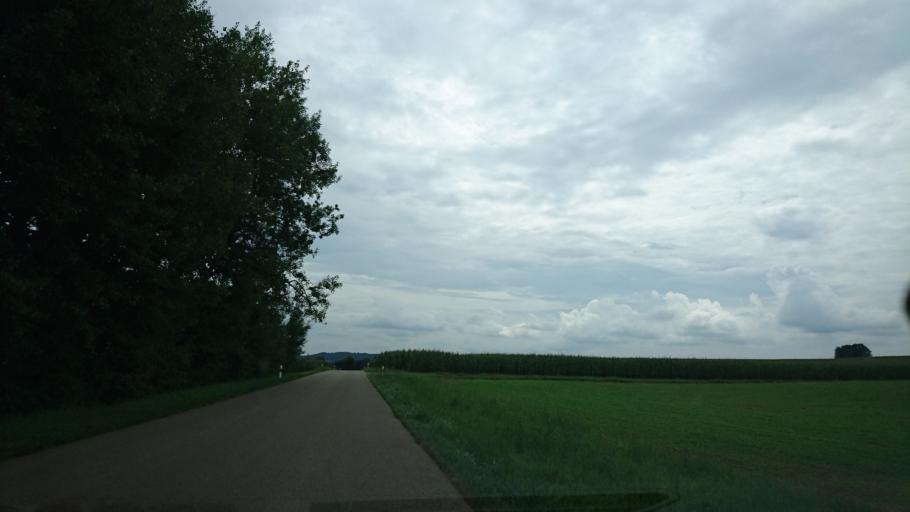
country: DE
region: Bavaria
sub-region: Swabia
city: Dinkelscherben
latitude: 48.3716
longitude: 10.5711
